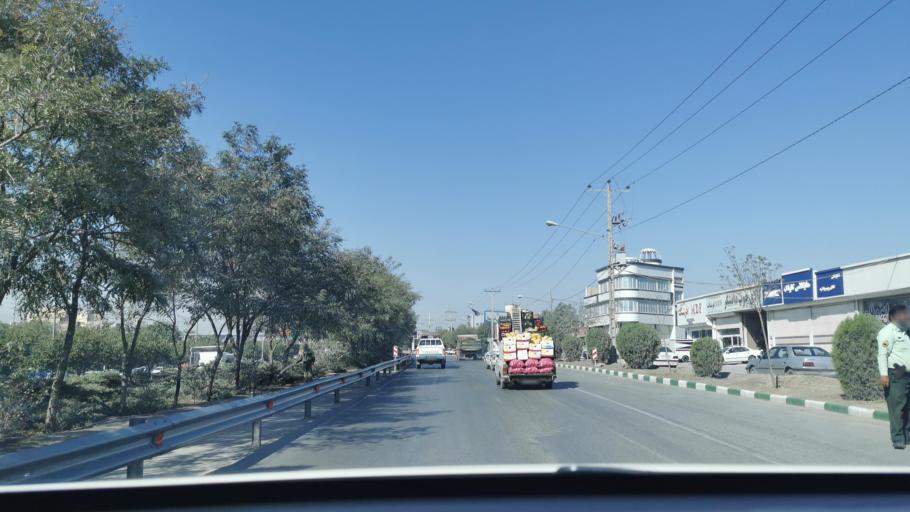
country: IR
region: Razavi Khorasan
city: Mashhad
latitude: 36.3503
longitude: 59.5739
